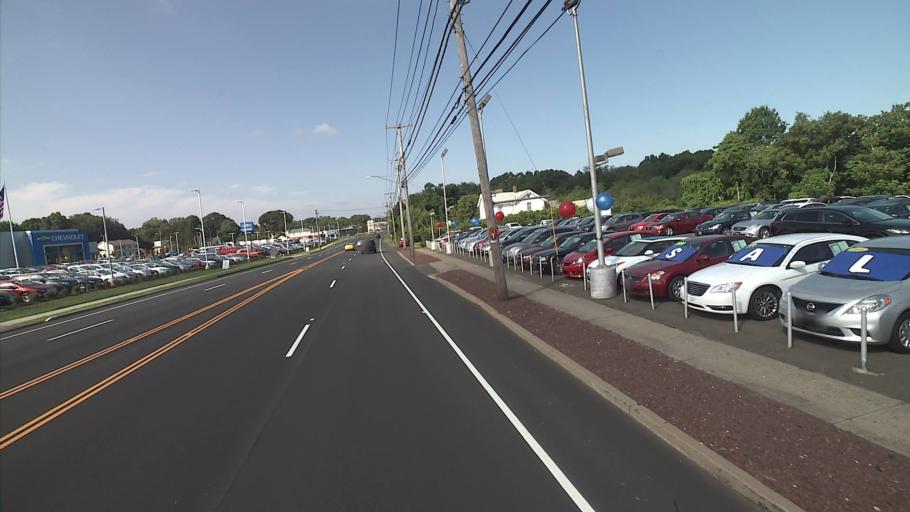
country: US
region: Connecticut
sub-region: New Haven County
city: City of Milford (balance)
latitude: 41.2094
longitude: -73.0838
